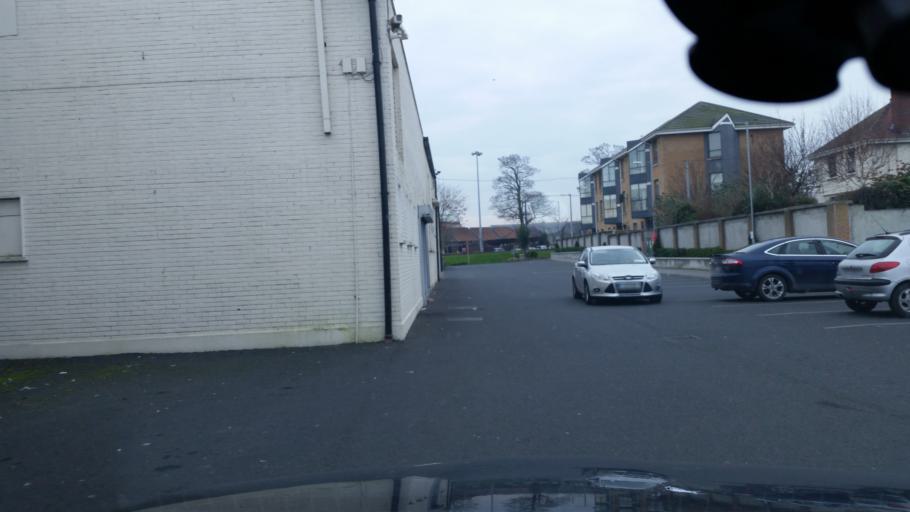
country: IE
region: Leinster
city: Artane
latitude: 53.3849
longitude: -6.2143
